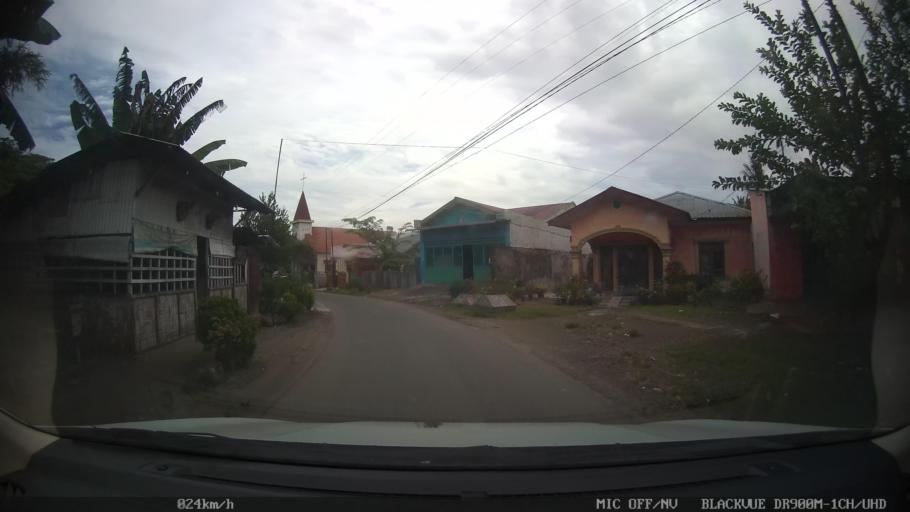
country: ID
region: North Sumatra
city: Sunggal
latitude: 3.5892
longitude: 98.5672
